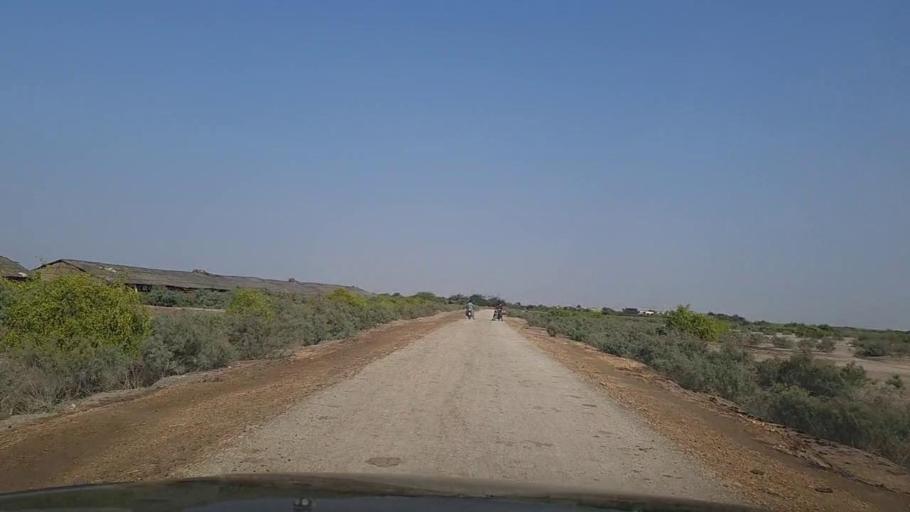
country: PK
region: Sindh
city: Thatta
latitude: 24.6449
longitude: 67.8163
